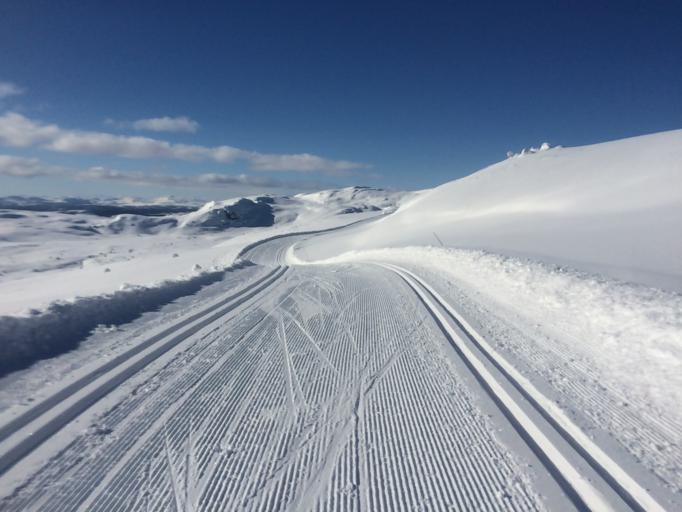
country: NO
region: Oppland
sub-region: Ringebu
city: Ringebu
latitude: 61.3710
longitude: 10.0736
